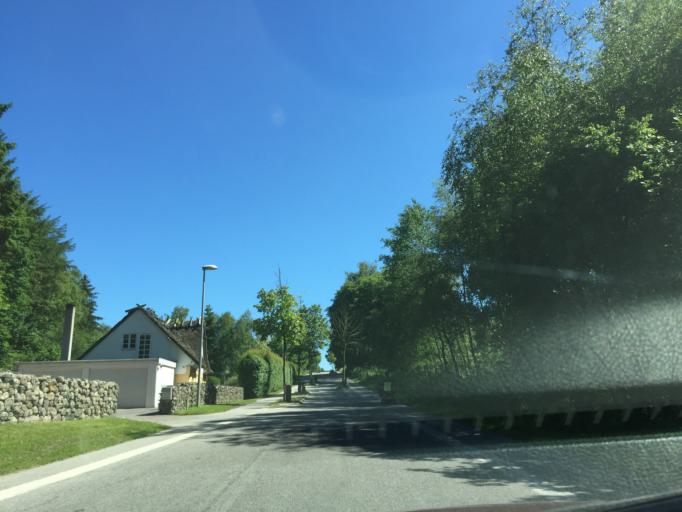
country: DK
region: Central Jutland
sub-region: Viborg Kommune
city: Bjerringbro
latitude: 56.3621
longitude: 9.6635
